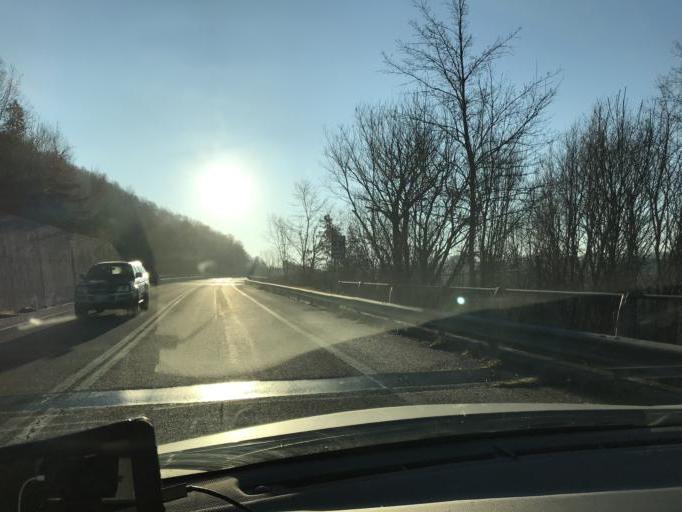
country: IT
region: Latium
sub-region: Provincia di Rieti
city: Petrella Salto
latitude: 42.2680
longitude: 13.0760
